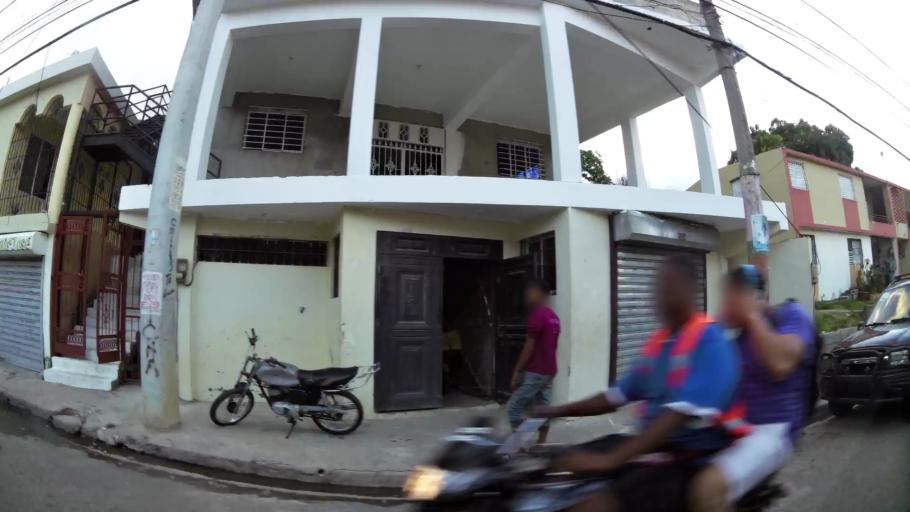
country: DO
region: Santo Domingo
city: Santo Domingo Oeste
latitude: 18.5263
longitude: -70.0187
